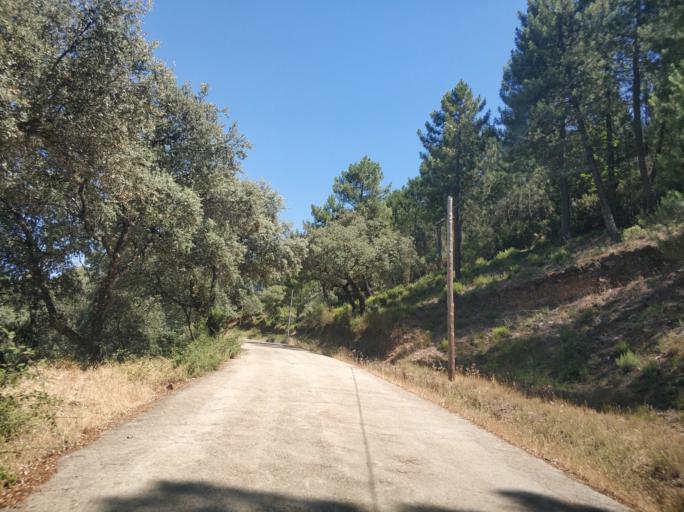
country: ES
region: Castille and Leon
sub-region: Provincia de Salamanca
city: Herguijuela de la Sierra
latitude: 40.4012
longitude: -6.0807
